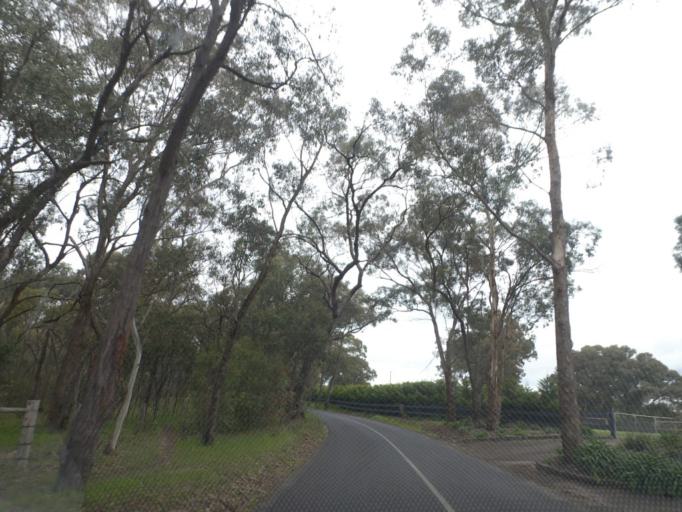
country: AU
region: Victoria
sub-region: Nillumbik
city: Hurstbridge
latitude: -37.6644
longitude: 145.2540
